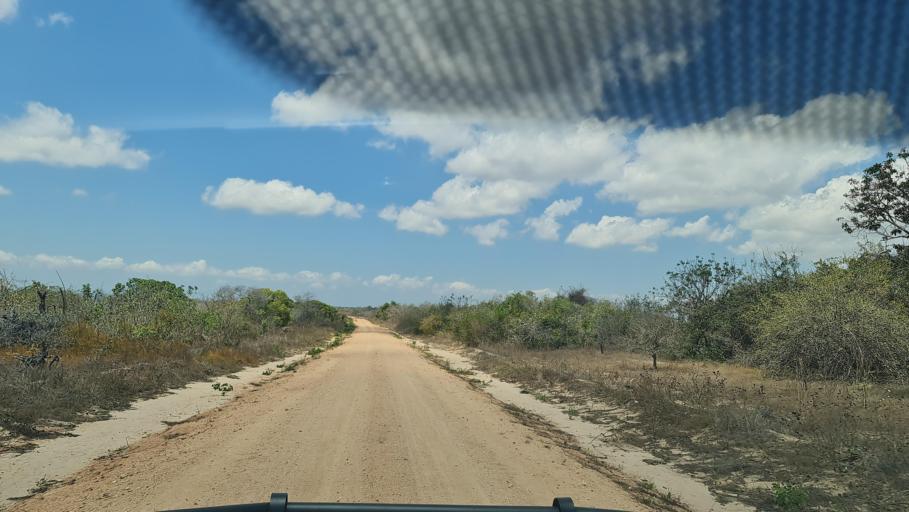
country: MZ
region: Nampula
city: Nacala
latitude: -14.3195
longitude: 40.5862
